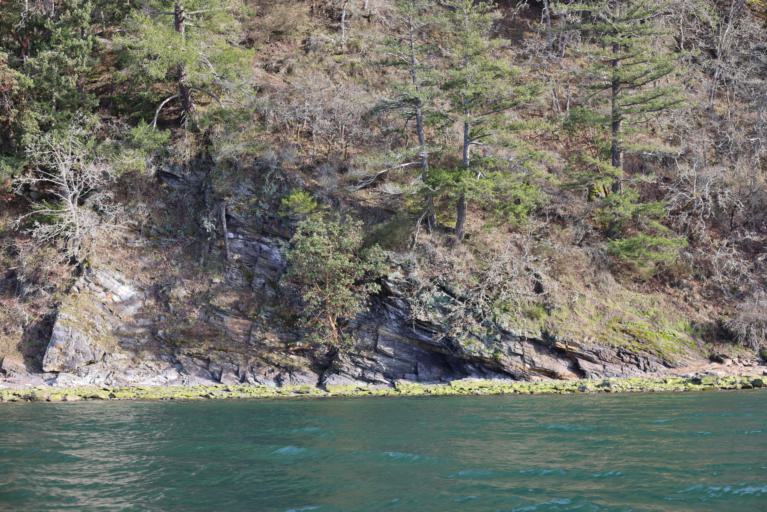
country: CA
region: British Columbia
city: Duncan
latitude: 48.7577
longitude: -123.6103
